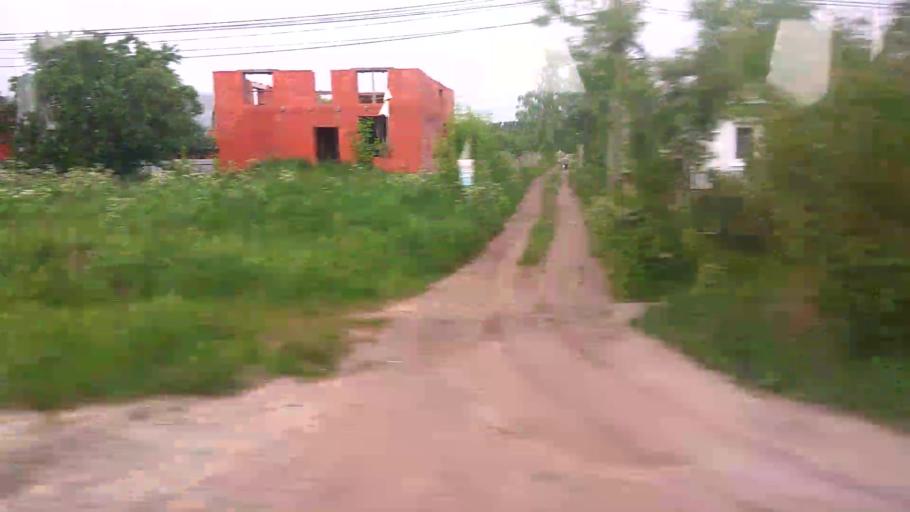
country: RU
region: Moskovskaya
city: Lukhovitsy
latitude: 54.9293
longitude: 39.0028
